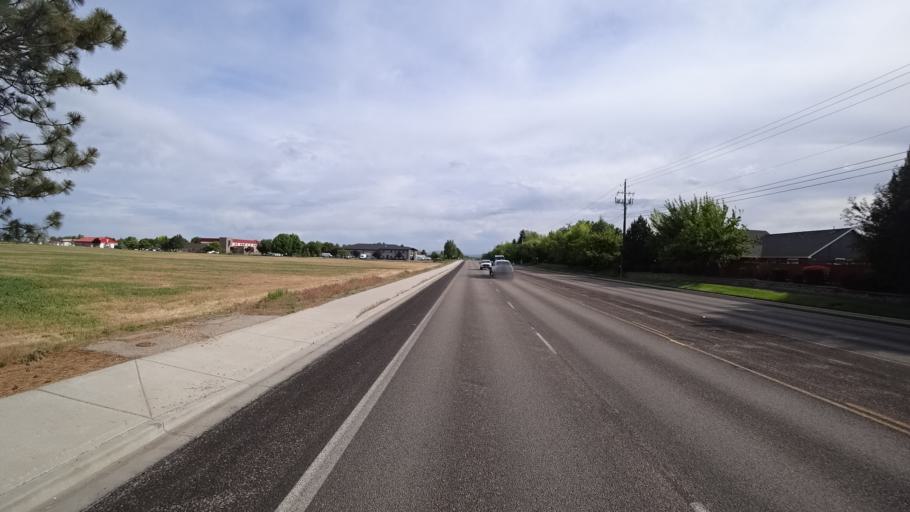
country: US
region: Idaho
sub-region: Ada County
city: Meridian
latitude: 43.5979
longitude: -116.3746
